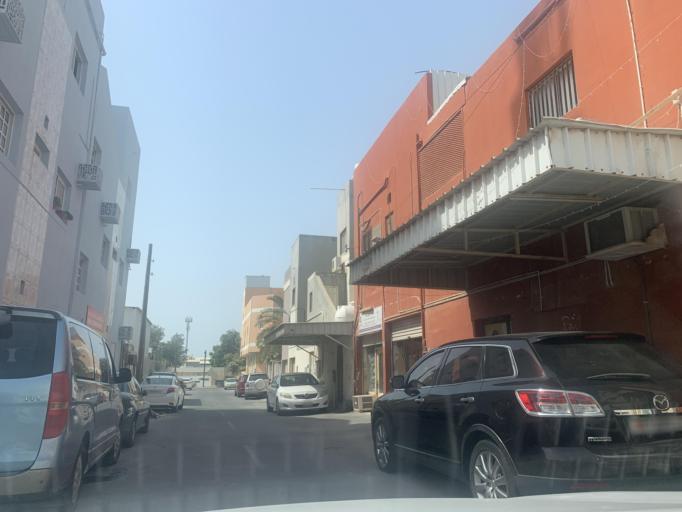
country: BH
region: Manama
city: Jidd Hafs
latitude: 26.2179
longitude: 50.4698
